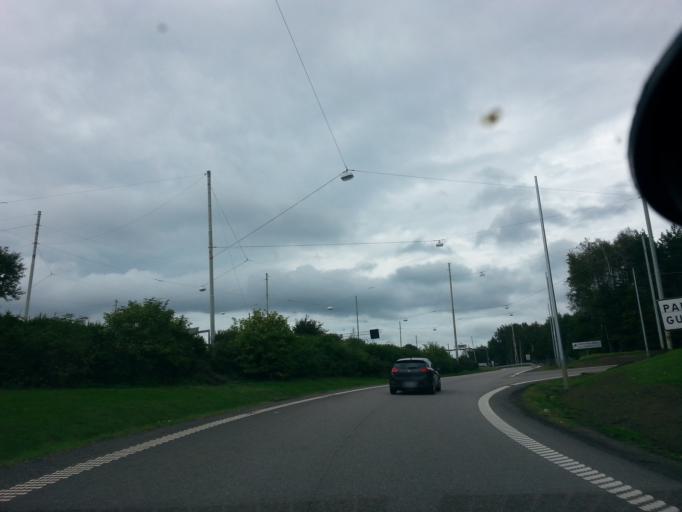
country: SE
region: Vaestra Goetaland
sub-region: Goteborg
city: Goeteborg
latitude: 57.7185
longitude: 11.9924
